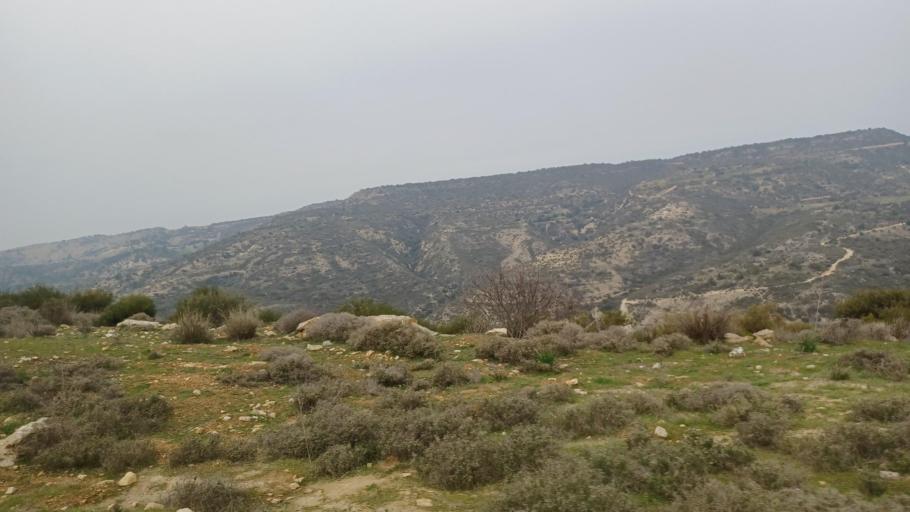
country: CY
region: Limassol
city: Pachna
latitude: 34.7546
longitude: 32.7411
